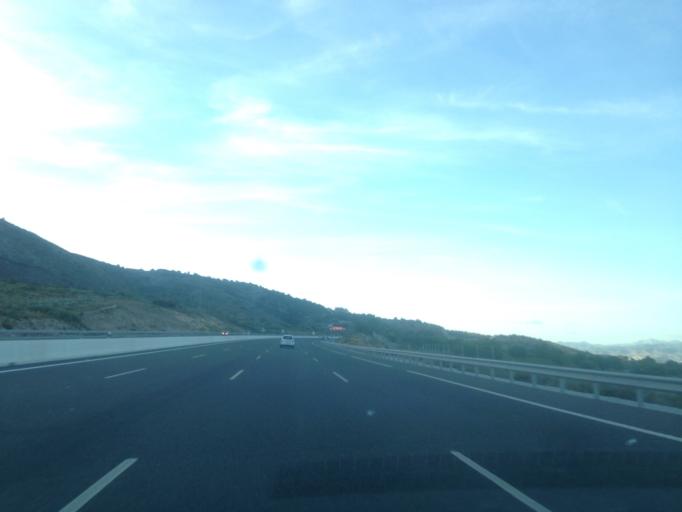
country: ES
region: Andalusia
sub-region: Provincia de Malaga
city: Torremolinos
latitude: 36.6349
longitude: -4.5134
